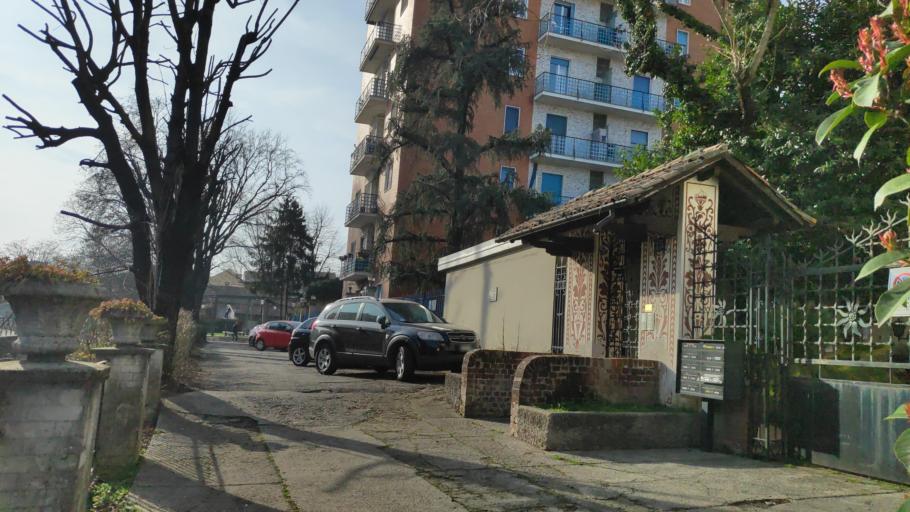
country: IT
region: Lombardy
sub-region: Citta metropolitana di Milano
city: Sesto San Giovanni
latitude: 45.5105
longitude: 9.2493
